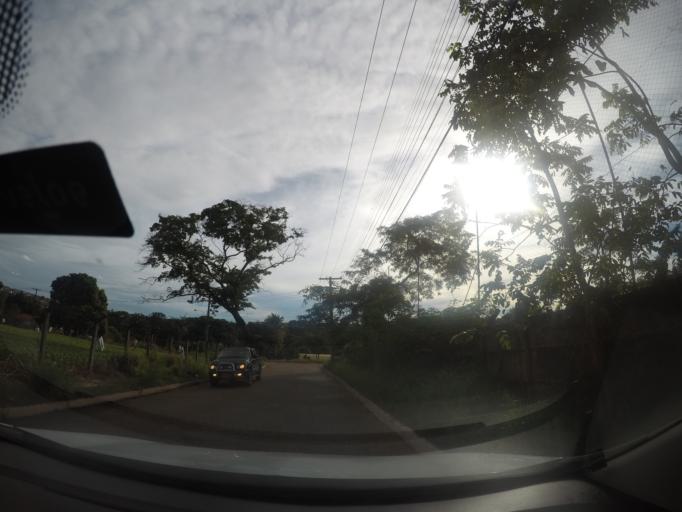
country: BR
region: Goias
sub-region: Goiania
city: Goiania
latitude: -16.6420
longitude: -49.3488
